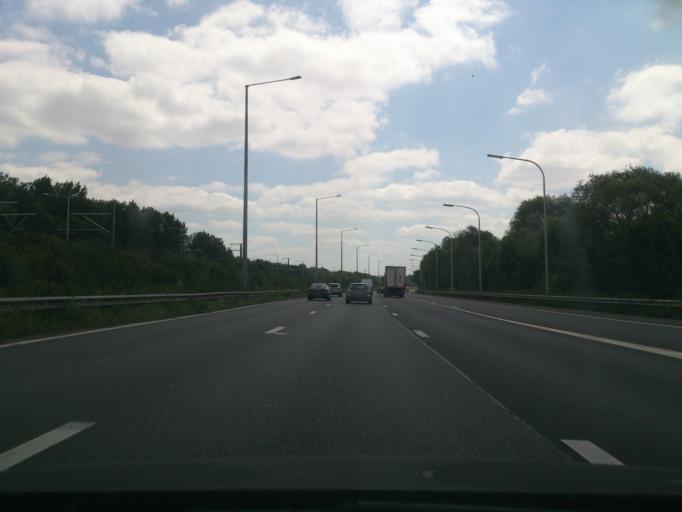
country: BE
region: Flanders
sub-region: Provincie Vlaams-Brabant
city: Zemst
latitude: 50.9724
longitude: 4.4899
